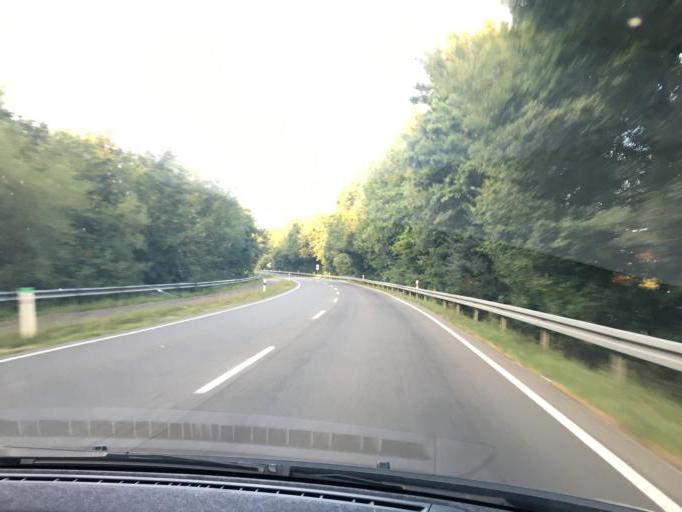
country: DE
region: North Rhine-Westphalia
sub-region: Regierungsbezirk Koln
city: Simmerath
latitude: 50.5848
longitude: 6.2719
